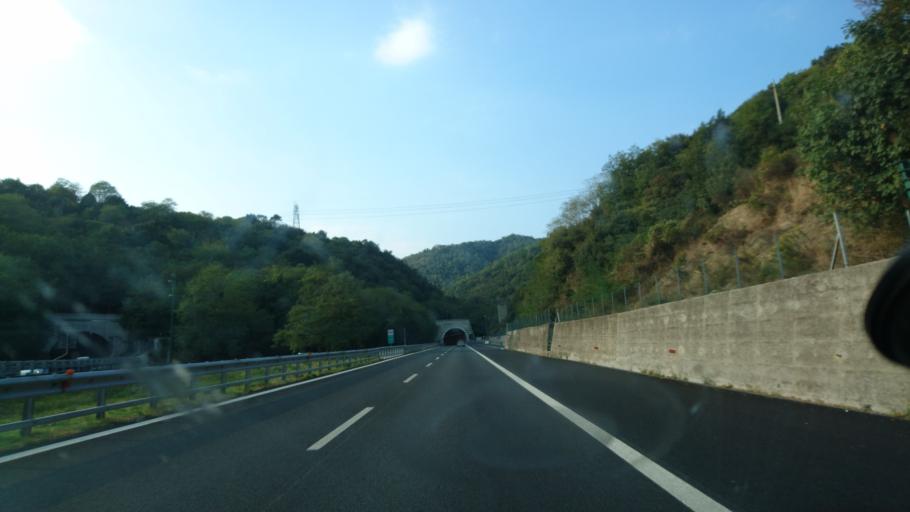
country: IT
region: Liguria
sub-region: Provincia di Savona
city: Quiliano
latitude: 44.2983
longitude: 8.4272
